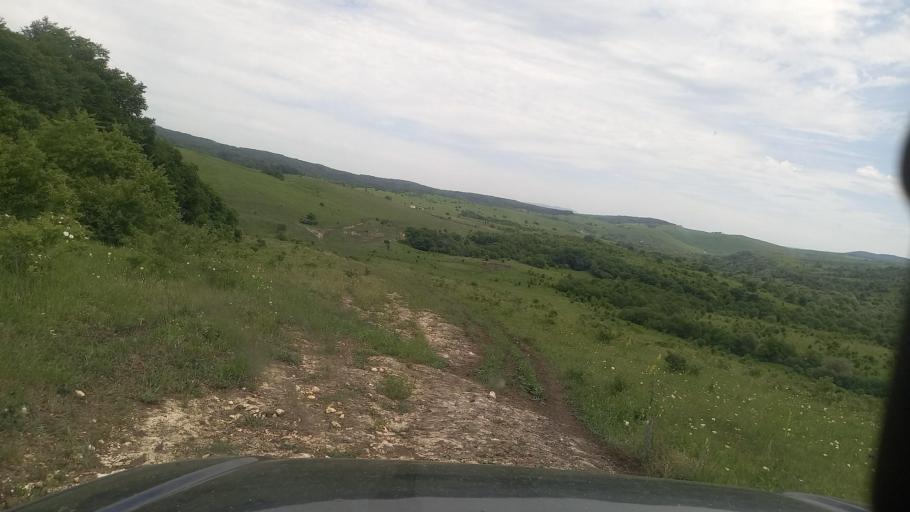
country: RU
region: Karachayevo-Cherkesiya
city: Pregradnaya
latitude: 44.0813
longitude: 41.2356
